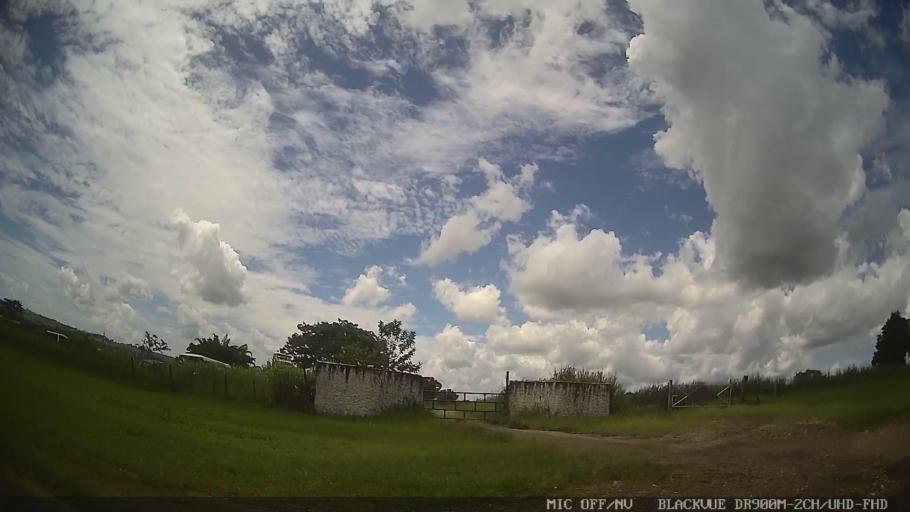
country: BR
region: Sao Paulo
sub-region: Laranjal Paulista
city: Laranjal Paulista
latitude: -23.0464
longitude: -47.9250
